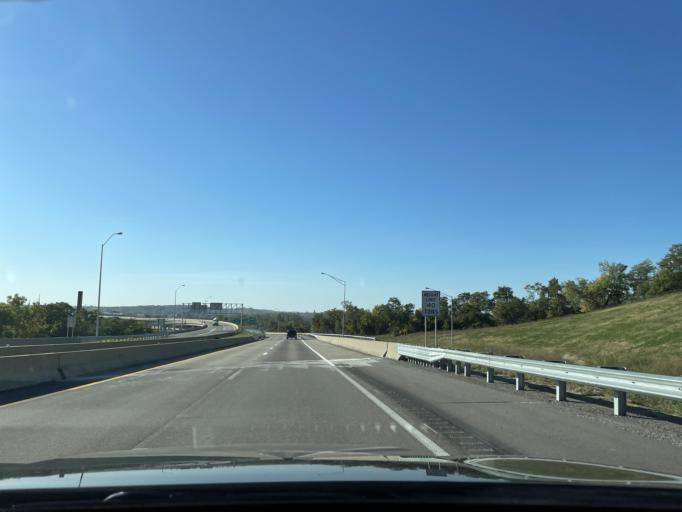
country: US
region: Missouri
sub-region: Buchanan County
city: Saint Joseph
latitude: 39.7711
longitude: -94.8615
